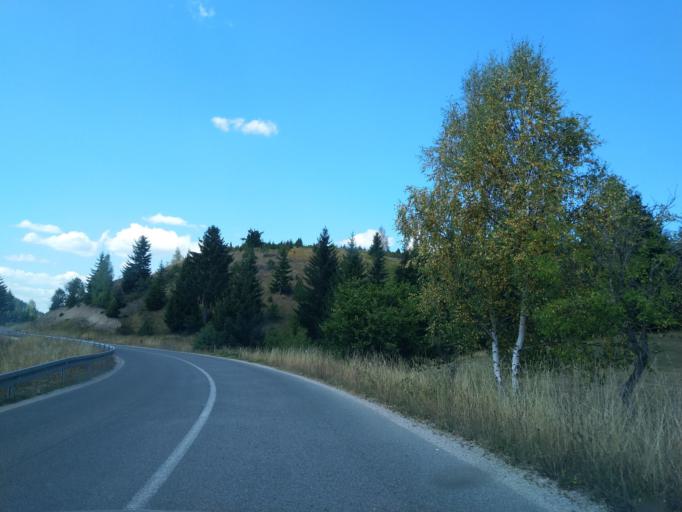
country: RS
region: Central Serbia
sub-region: Zlatiborski Okrug
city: Nova Varos
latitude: 43.4278
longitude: 19.8304
